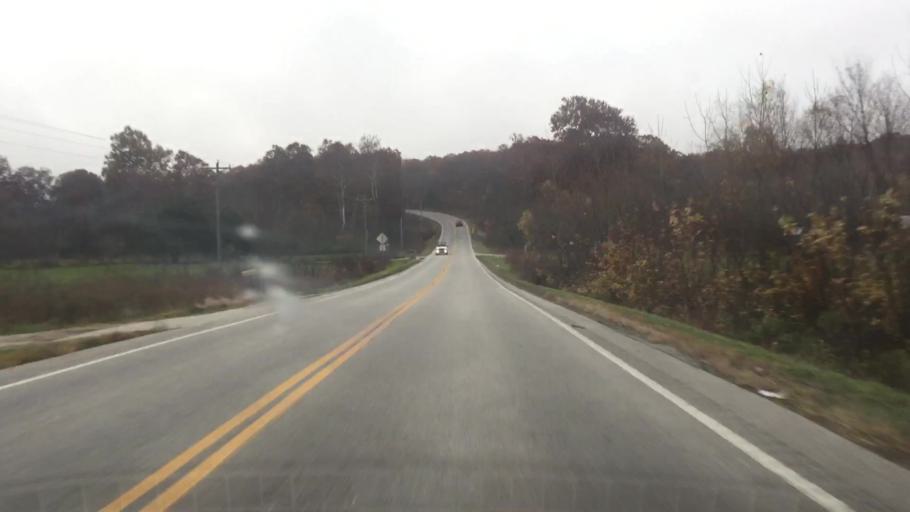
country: US
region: Missouri
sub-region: Callaway County
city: Fulton
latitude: 38.8817
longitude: -92.0906
